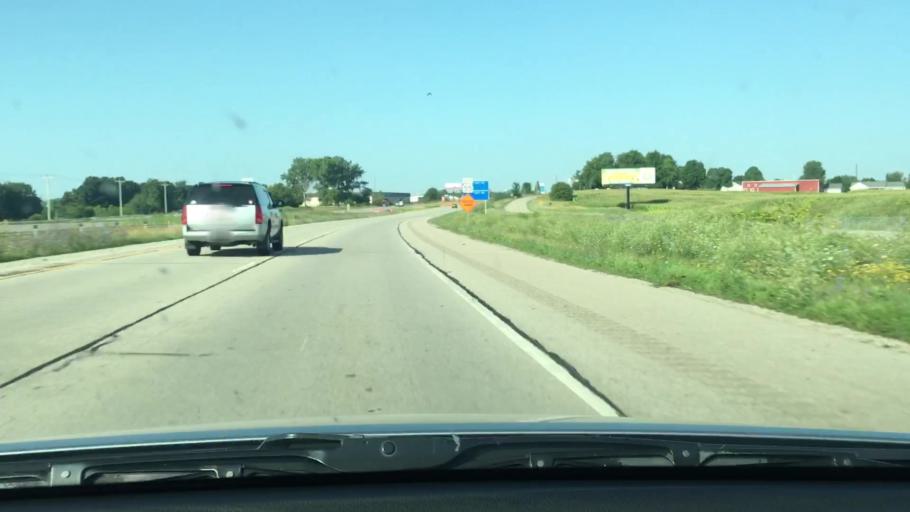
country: US
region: Wisconsin
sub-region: Outagamie County
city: Kaukauna
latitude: 44.3099
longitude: -88.2357
